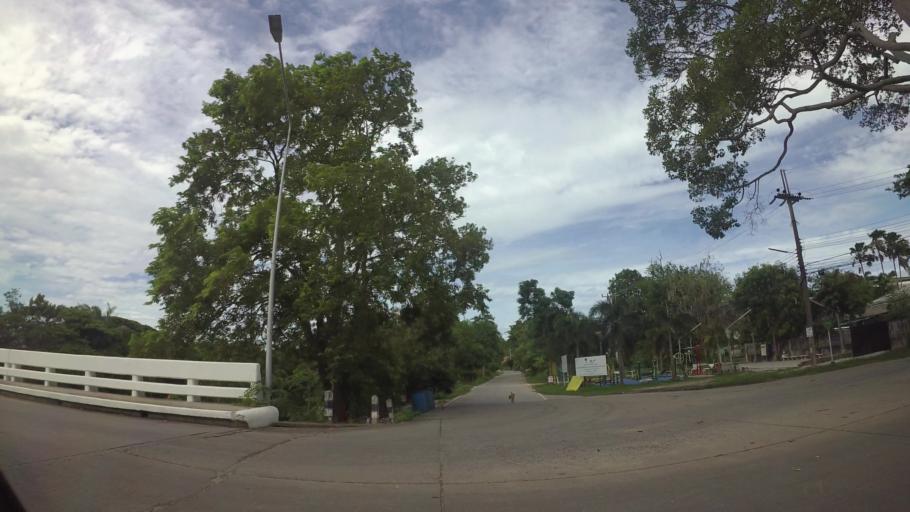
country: TH
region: Rayong
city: Rayong
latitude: 12.6825
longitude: 101.2614
